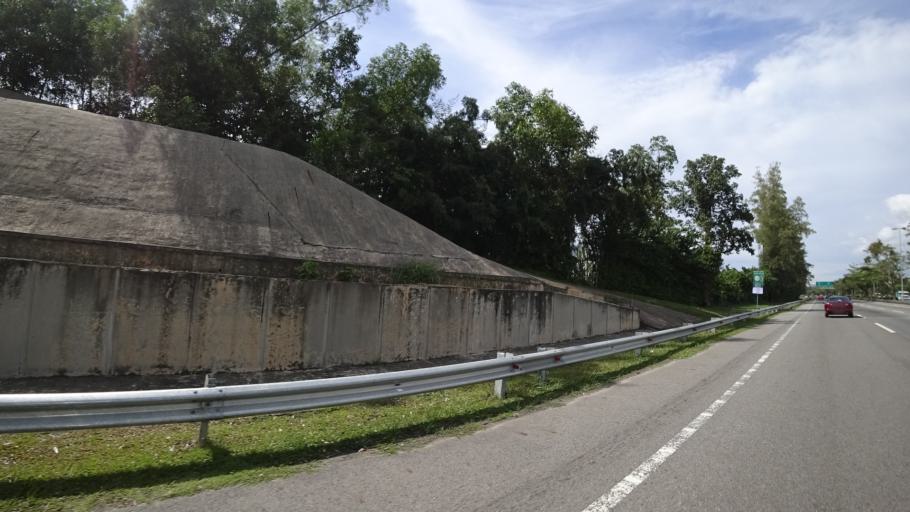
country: BN
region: Brunei and Muara
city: Bandar Seri Begawan
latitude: 4.9349
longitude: 114.9294
